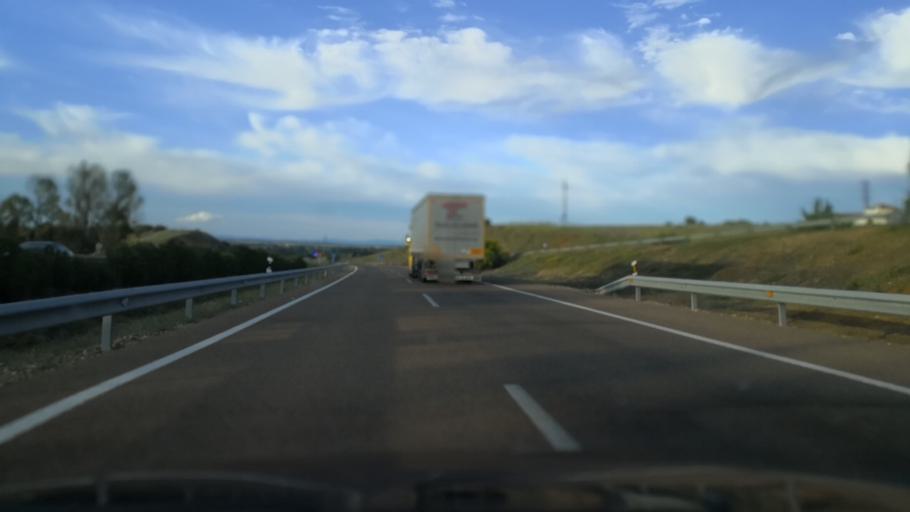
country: ES
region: Extremadura
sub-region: Provincia de Badajoz
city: Lobon
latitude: 38.8439
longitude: -6.6197
